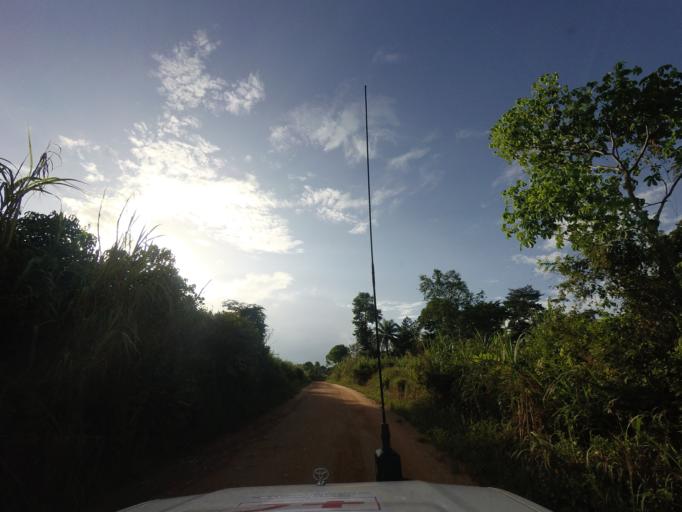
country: GN
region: Nzerekore
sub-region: Nzerekore Prefecture
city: Nzerekore
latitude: 7.6918
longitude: -8.8192
